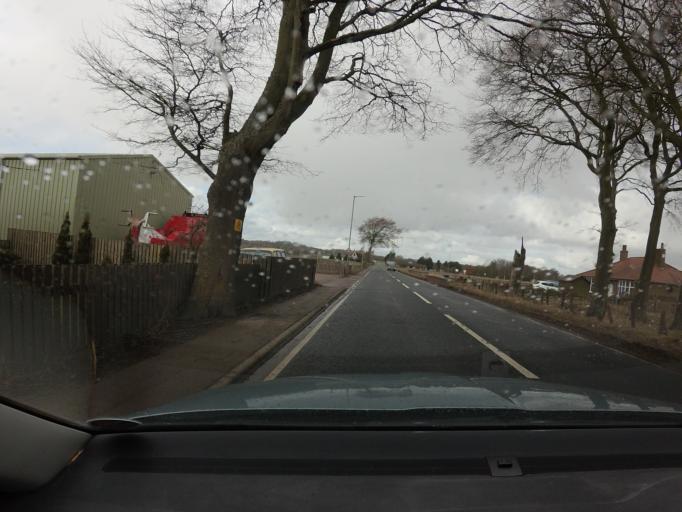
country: GB
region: Scotland
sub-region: South Lanarkshire
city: Lanark
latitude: 55.6845
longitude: -3.7151
